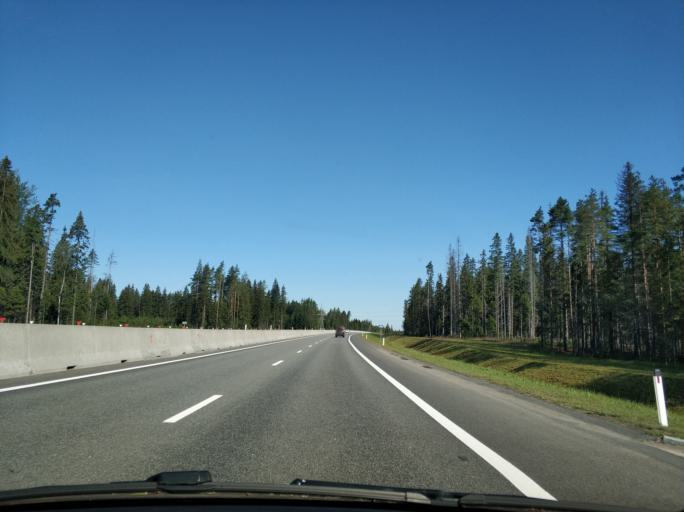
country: RU
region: Leningrad
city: Sosnovo
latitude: 60.5207
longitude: 30.1731
